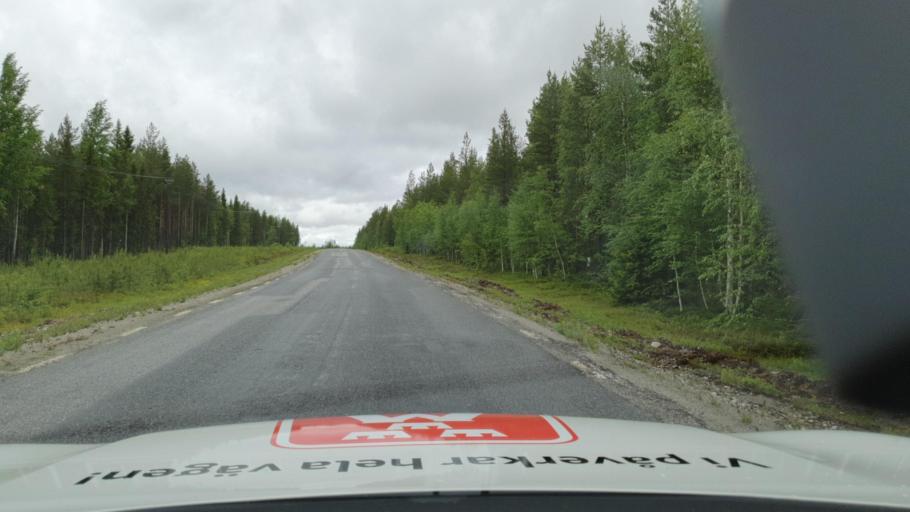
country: SE
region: Vaesterbotten
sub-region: Dorotea Kommun
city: Dorotea
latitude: 64.1443
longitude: 16.6480
